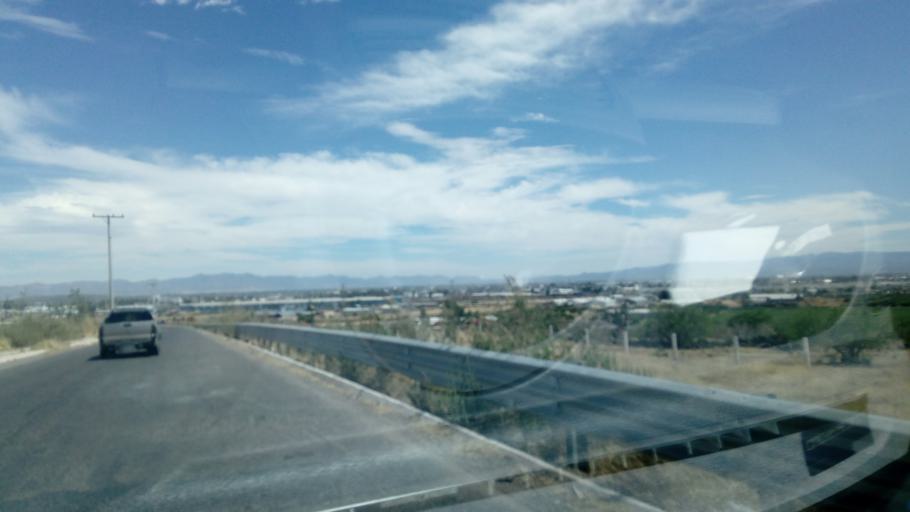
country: MX
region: Durango
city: Victoria de Durango
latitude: 24.0763
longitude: -104.6213
